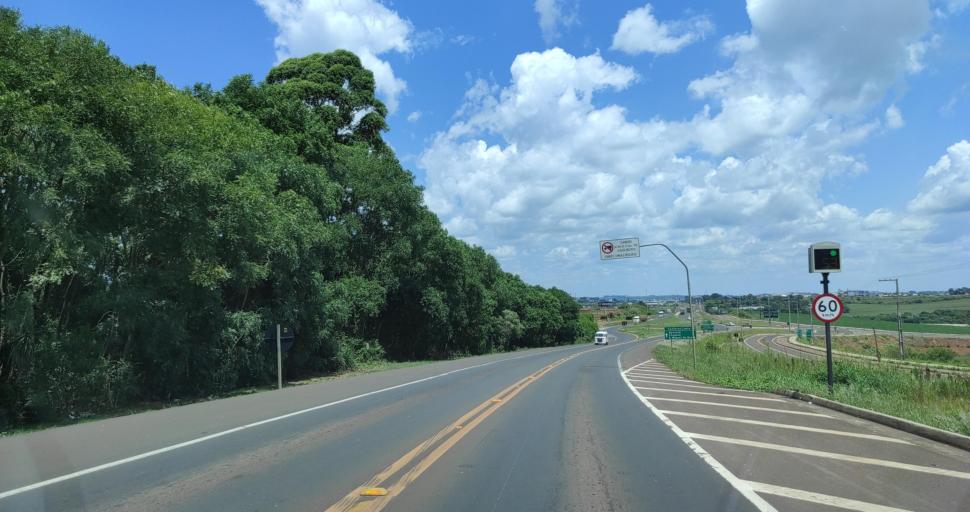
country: BR
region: Santa Catarina
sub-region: Xanxere
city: Xanxere
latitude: -26.8804
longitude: -52.3562
